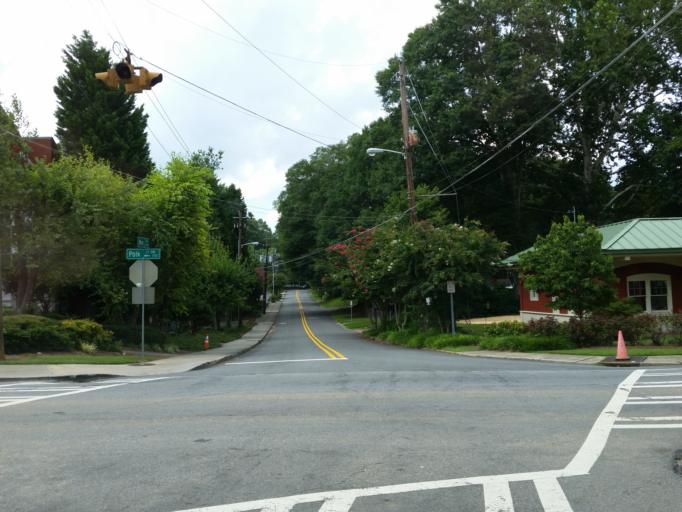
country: US
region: Georgia
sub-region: Cobb County
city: Marietta
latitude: 33.9554
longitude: -84.5569
